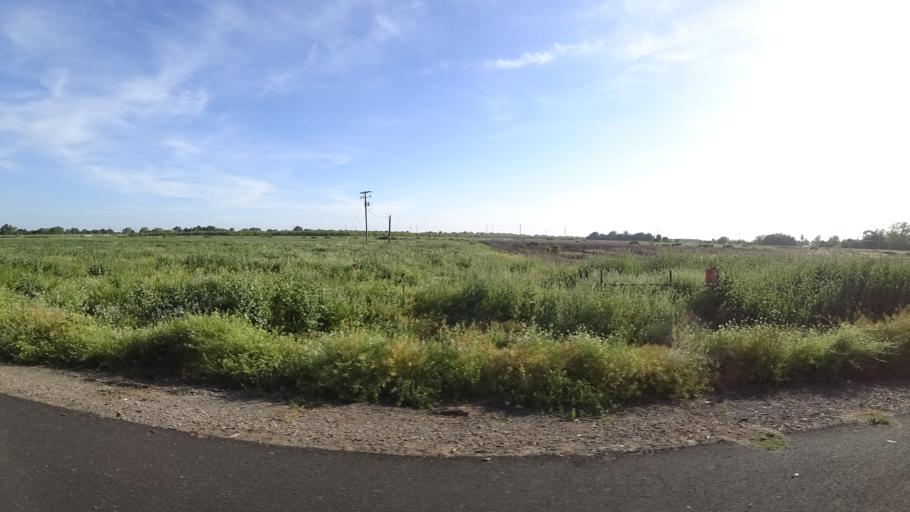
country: US
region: California
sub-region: Yuba County
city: Wheatland
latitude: 39.0067
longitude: -121.4179
